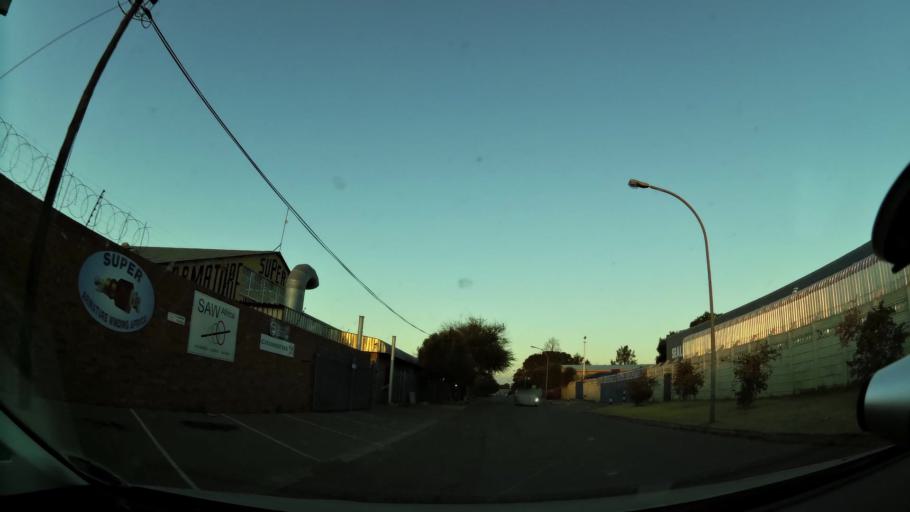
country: ZA
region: Northern Cape
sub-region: Frances Baard District Municipality
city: Kimberley
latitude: -28.7283
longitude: 24.7710
